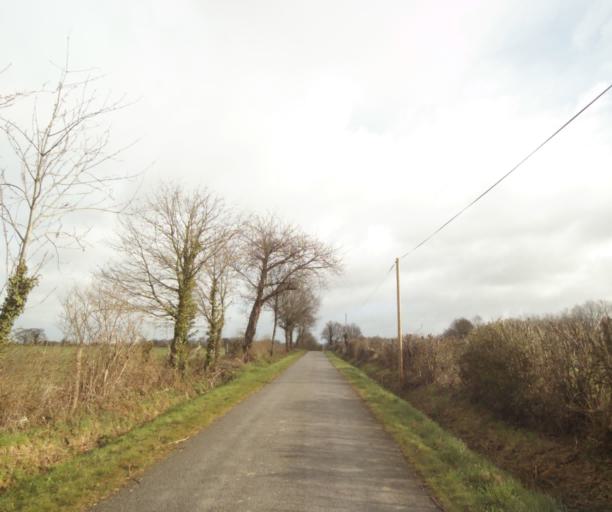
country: FR
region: Pays de la Loire
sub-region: Departement de la Loire-Atlantique
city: Bouvron
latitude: 47.3978
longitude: -1.8609
